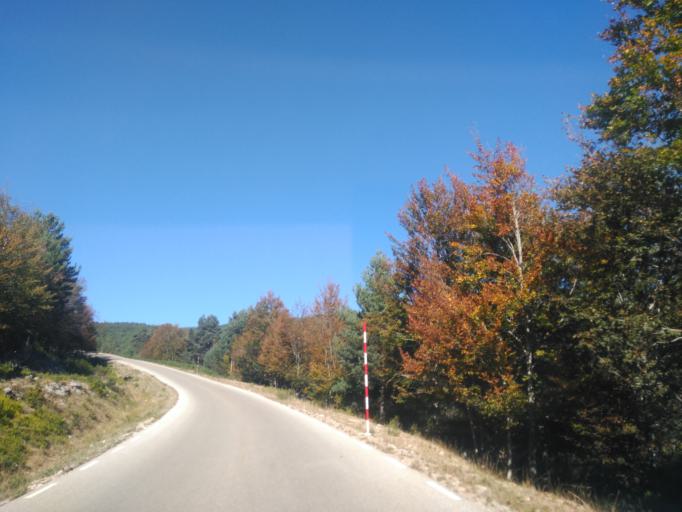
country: ES
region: La Rioja
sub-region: Provincia de La Rioja
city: Viniegra de Arriba
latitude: 42.0173
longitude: -2.8147
